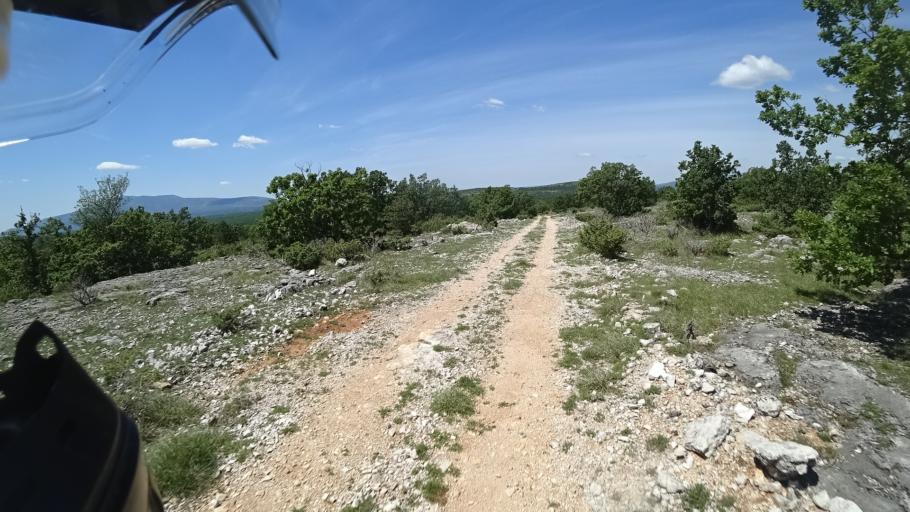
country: HR
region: Sibensko-Kniniska
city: Knin
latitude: 44.0321
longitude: 16.2774
